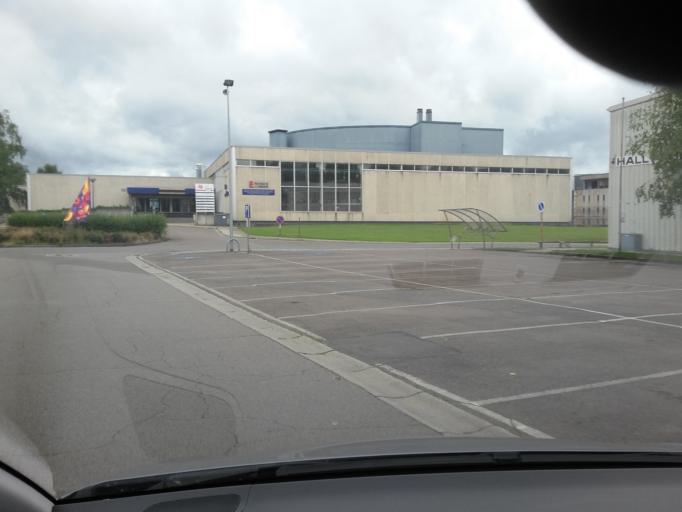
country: BE
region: Wallonia
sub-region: Province du Luxembourg
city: Arlon
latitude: 49.6798
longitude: 5.8029
